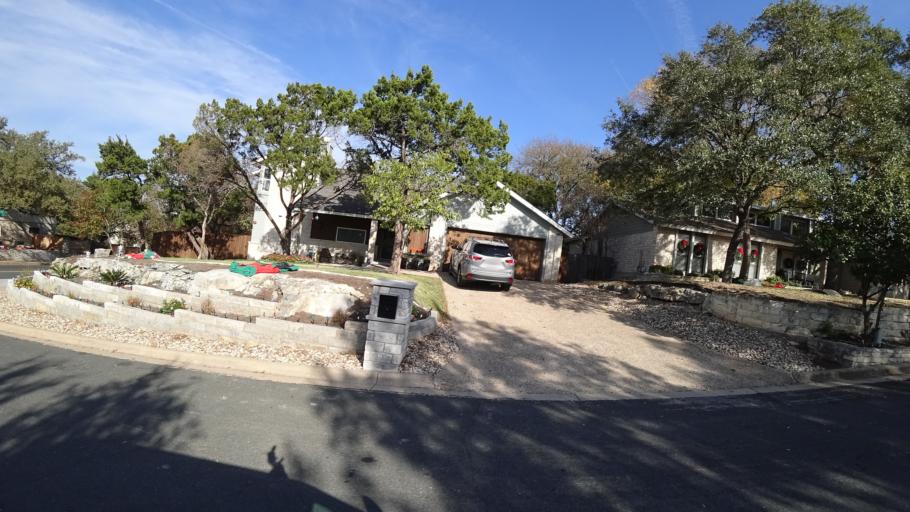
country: US
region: Texas
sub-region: Williamson County
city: Jollyville
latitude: 30.3806
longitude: -97.7557
